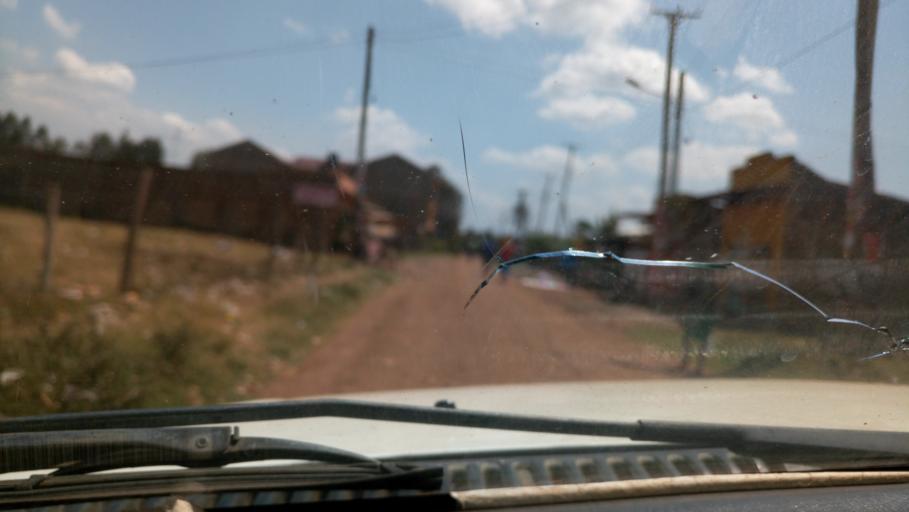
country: KE
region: Nairobi Area
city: Thika
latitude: -0.9342
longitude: 37.1207
